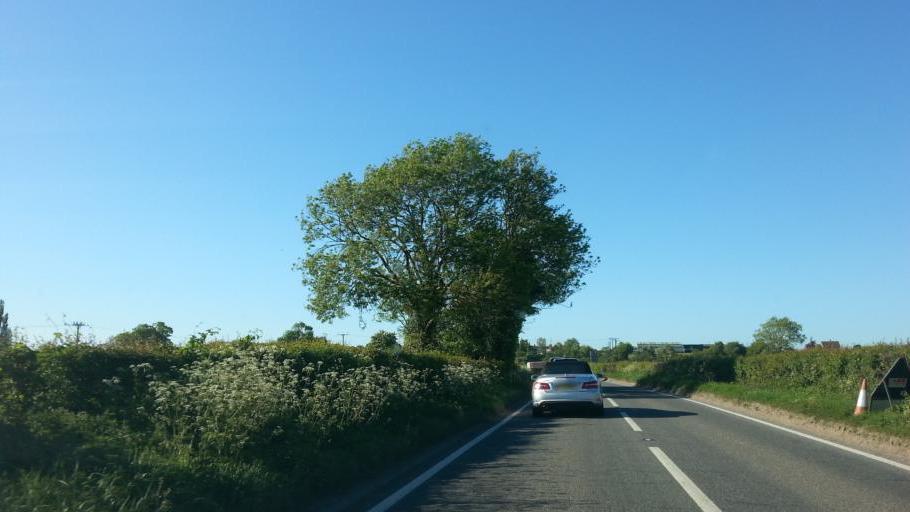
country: GB
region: England
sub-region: Somerset
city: Evercreech
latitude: 51.1238
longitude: -2.5162
